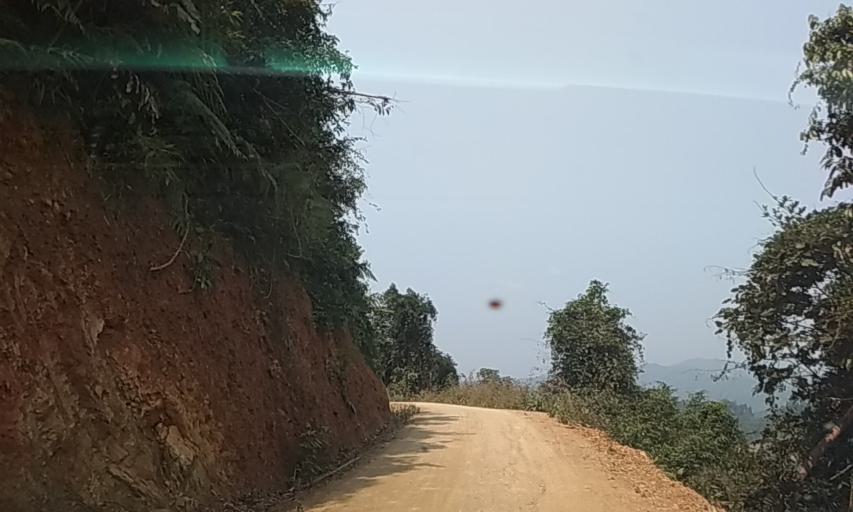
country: LA
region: Phongsali
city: Phongsali
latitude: 21.4712
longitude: 102.4277
